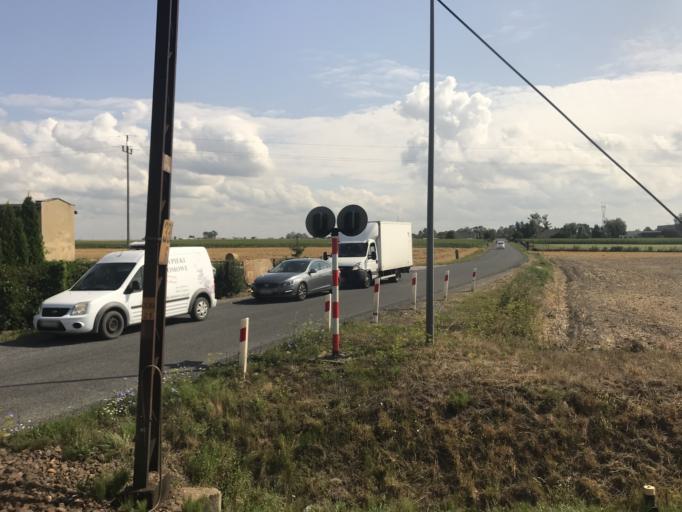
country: PL
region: Kujawsko-Pomorskie
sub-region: Powiat inowroclawski
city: Zlotniki Kujawskie
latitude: 52.9166
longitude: 18.1332
